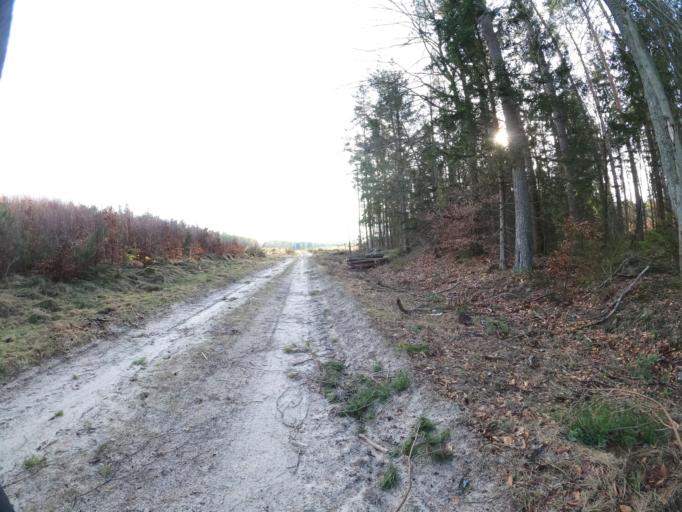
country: PL
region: West Pomeranian Voivodeship
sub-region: Powiat koszalinski
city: Polanow
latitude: 54.2147
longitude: 16.6432
